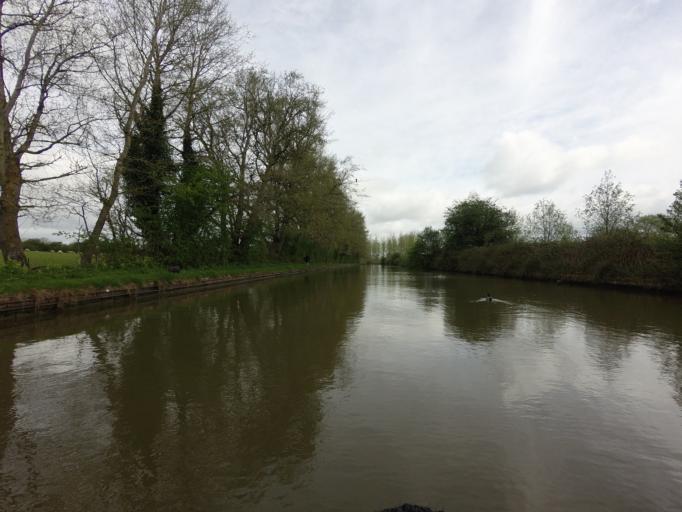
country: GB
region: England
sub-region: Milton Keynes
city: Water Eaton
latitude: 51.9517
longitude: -0.7077
